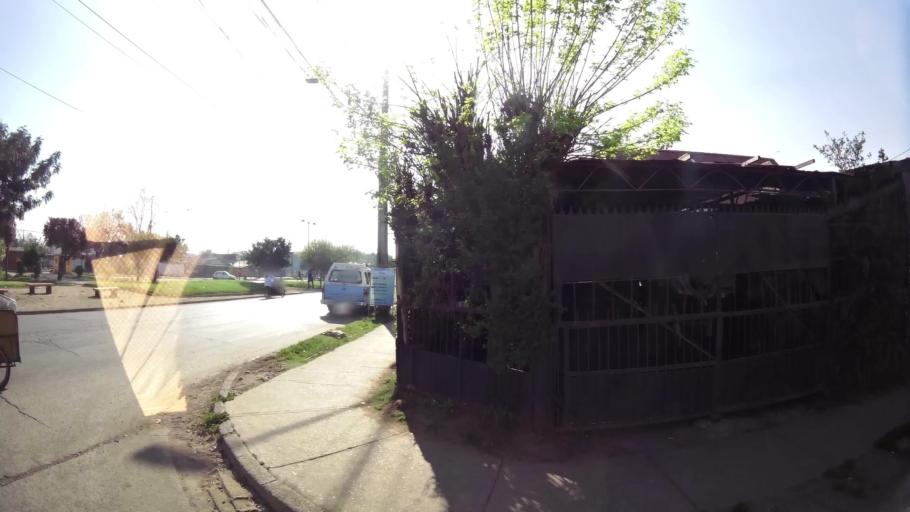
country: CL
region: Santiago Metropolitan
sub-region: Provincia de Santiago
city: Lo Prado
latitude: -33.4226
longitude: -70.7546
